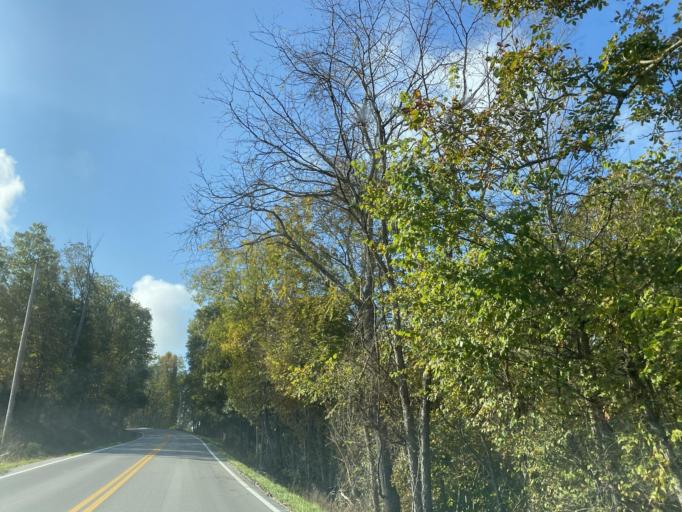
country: US
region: Kentucky
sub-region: Pendleton County
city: Falmouth
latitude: 38.6989
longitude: -84.3044
